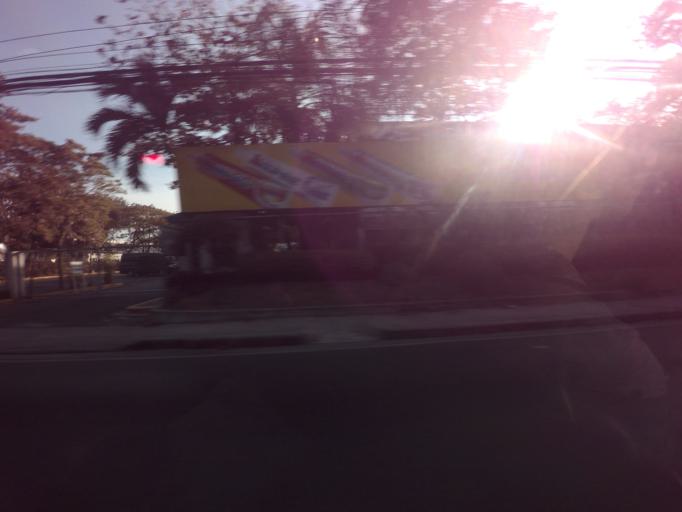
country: PH
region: Calabarzon
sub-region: Province of Rizal
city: Taguig
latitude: 14.4980
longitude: 121.0395
